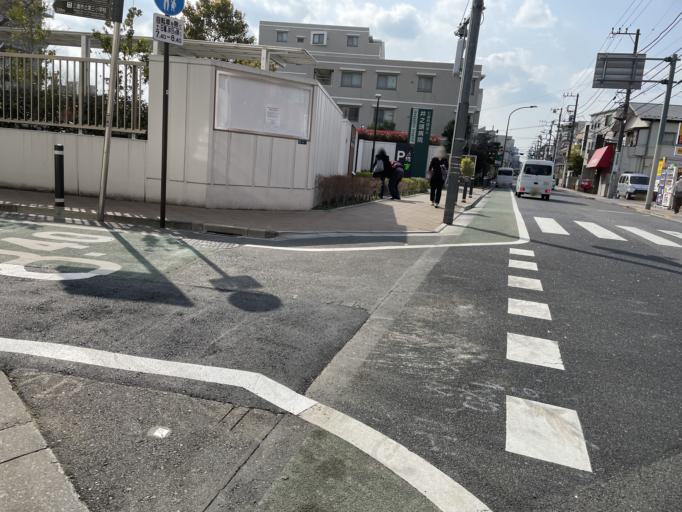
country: JP
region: Tokyo
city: Kamirenjaku
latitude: 35.6984
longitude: 139.5581
